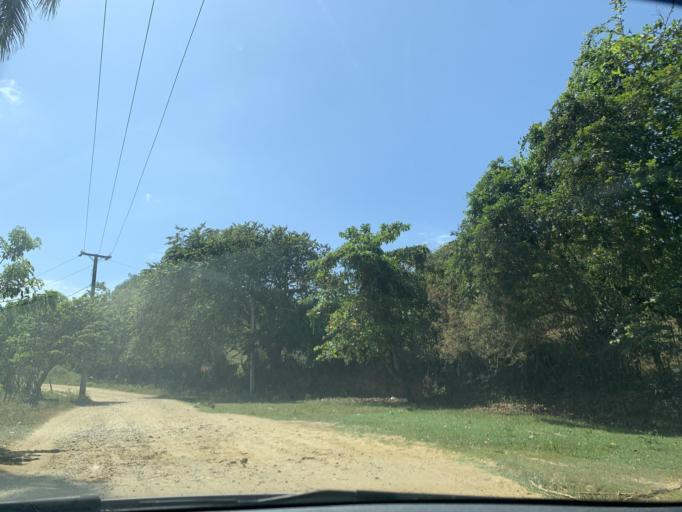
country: DO
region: Puerto Plata
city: Luperon
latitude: 19.8829
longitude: -70.8696
